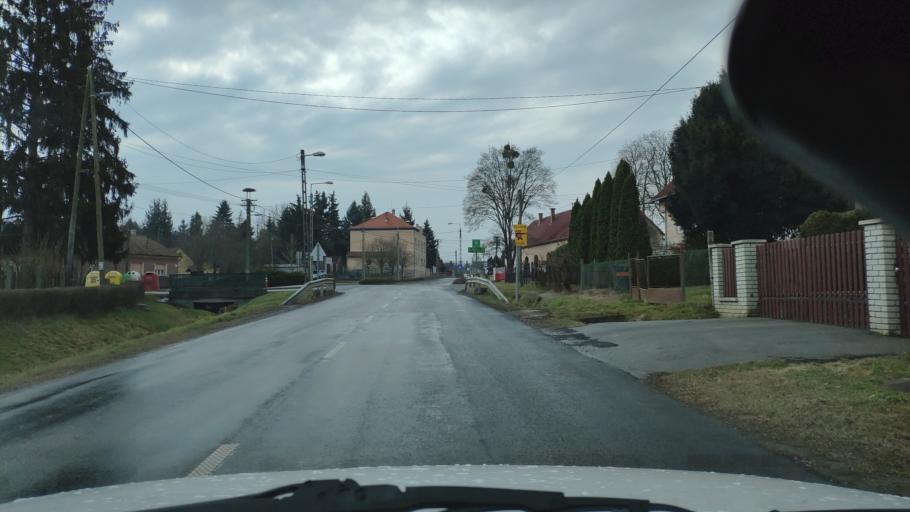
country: HU
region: Zala
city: Nagykanizsa
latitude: 46.4121
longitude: 16.9847
